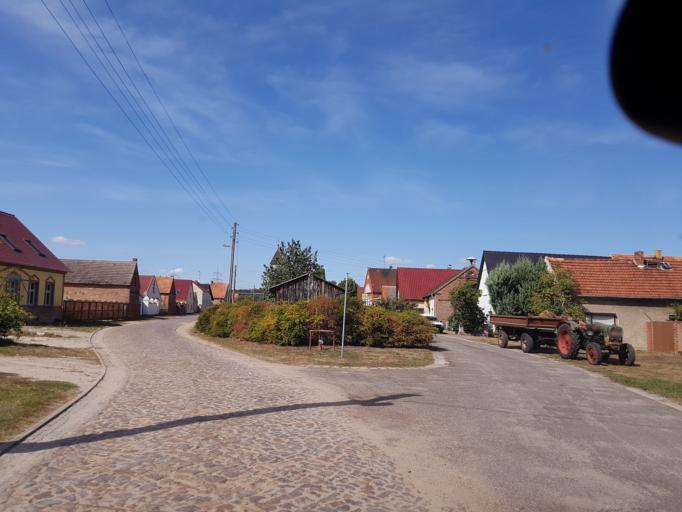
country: DE
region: Brandenburg
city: Luckau
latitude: 51.8642
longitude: 13.6482
